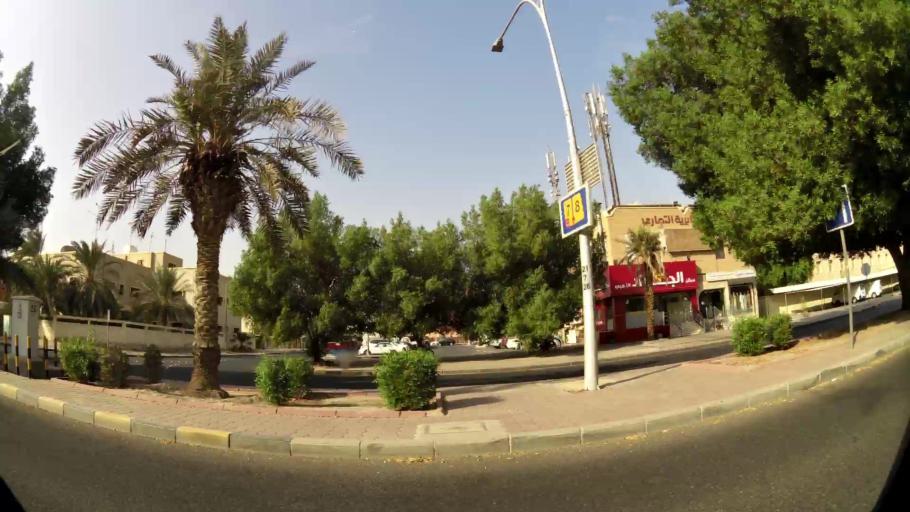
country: KW
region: Muhafazat Hawalli
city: Hawalli
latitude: 29.3243
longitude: 48.0377
